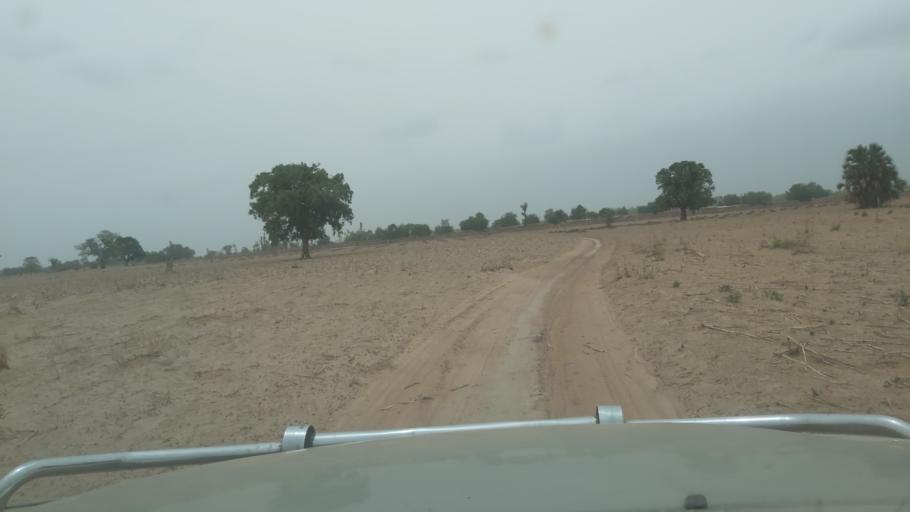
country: ML
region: Koulikoro
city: Banamba
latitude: 13.3765
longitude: -7.2272
